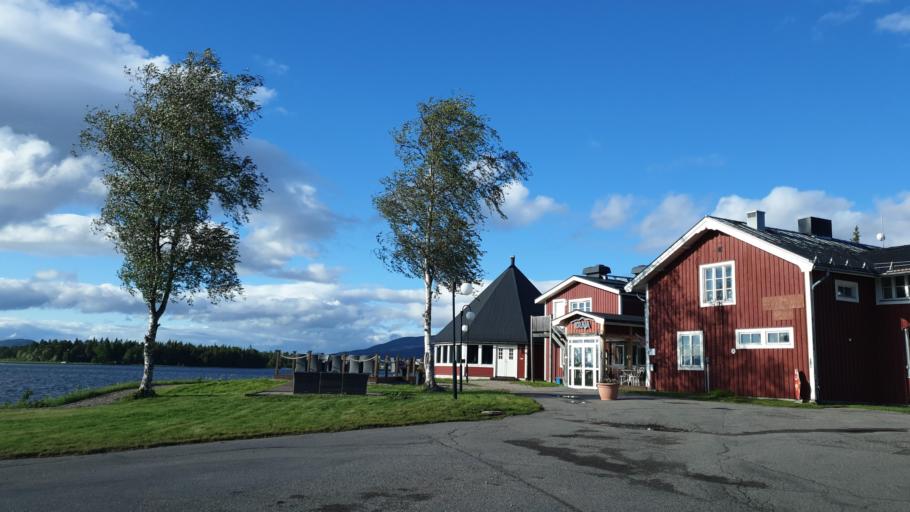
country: SE
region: Norrbotten
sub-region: Arjeplogs Kommun
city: Arjeplog
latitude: 66.0529
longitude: 17.8661
